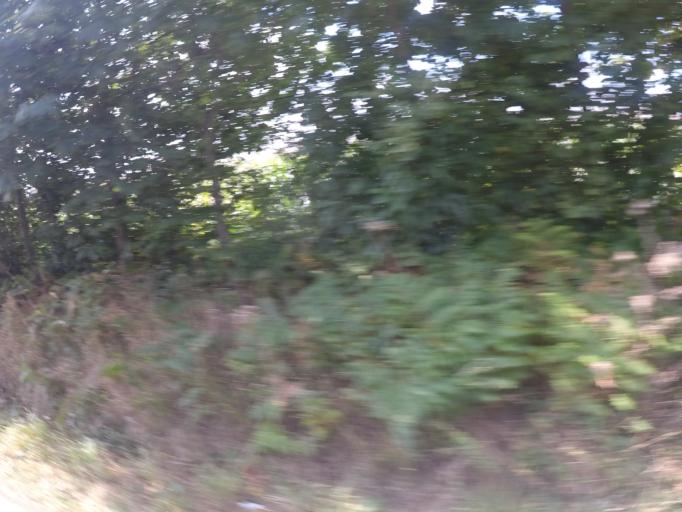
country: FR
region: Brittany
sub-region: Departement des Cotes-d'Armor
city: Tremuson
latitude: 48.5538
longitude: -2.8918
